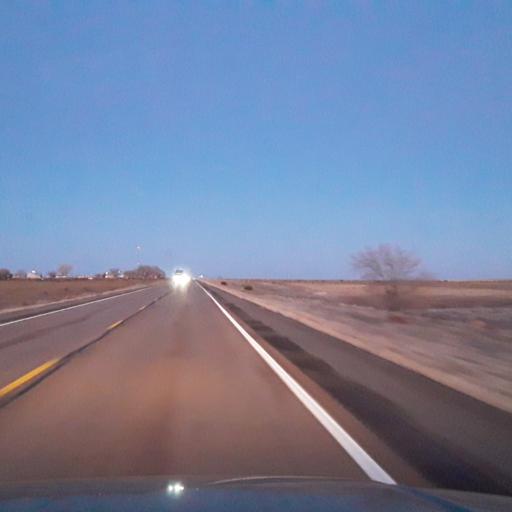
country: US
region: New Mexico
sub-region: Guadalupe County
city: Santa Rosa
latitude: 34.7773
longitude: -104.9506
